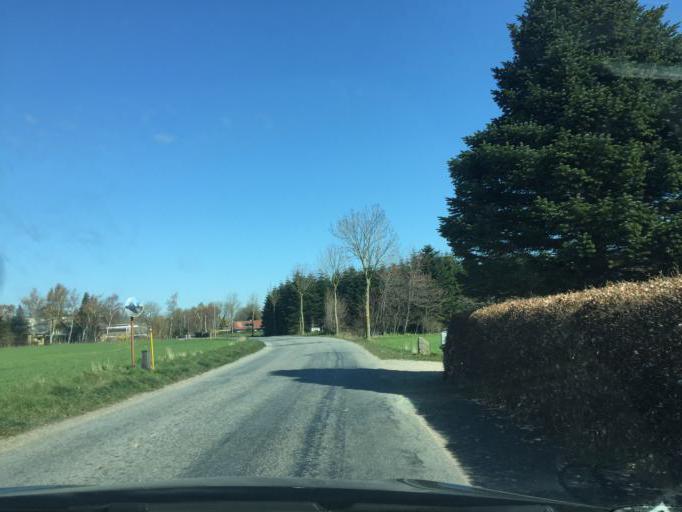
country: DK
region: South Denmark
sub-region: Faaborg-Midtfyn Kommune
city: Arslev
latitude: 55.2821
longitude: 10.5365
